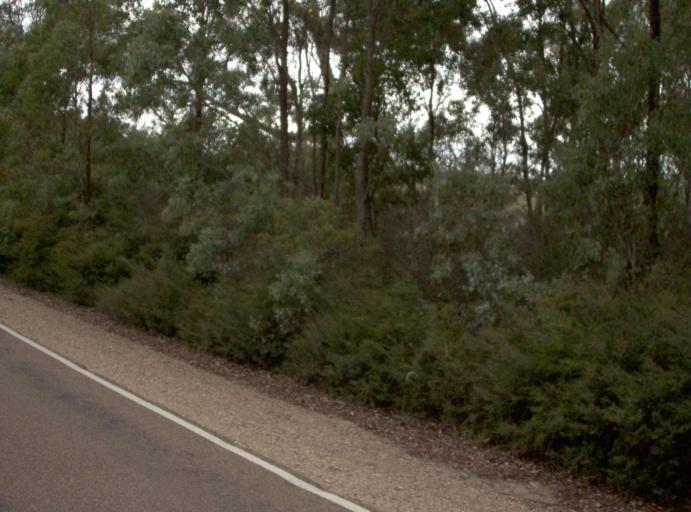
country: AU
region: Victoria
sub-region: Wellington
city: Sale
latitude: -38.0042
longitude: 147.2898
